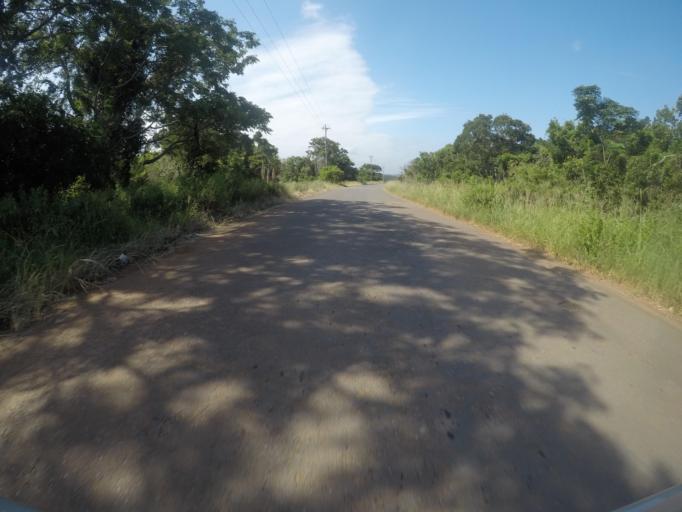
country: ZA
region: Eastern Cape
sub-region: Buffalo City Metropolitan Municipality
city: East London
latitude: -32.9660
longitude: 27.8751
